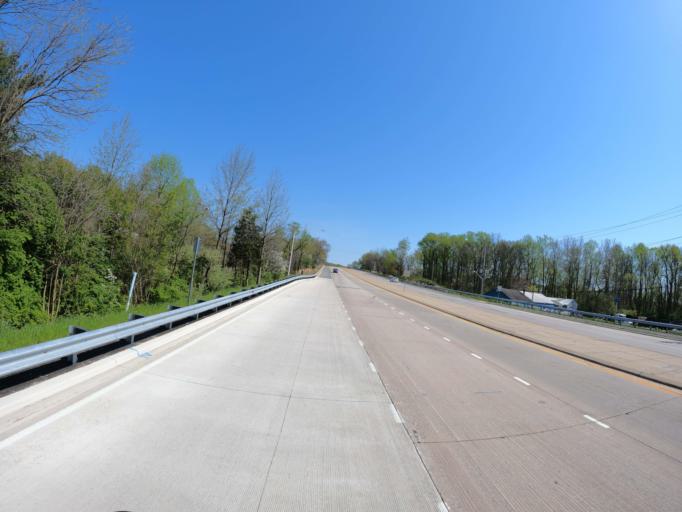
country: US
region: Delaware
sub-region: New Castle County
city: Newark
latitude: 39.6572
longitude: -75.7838
